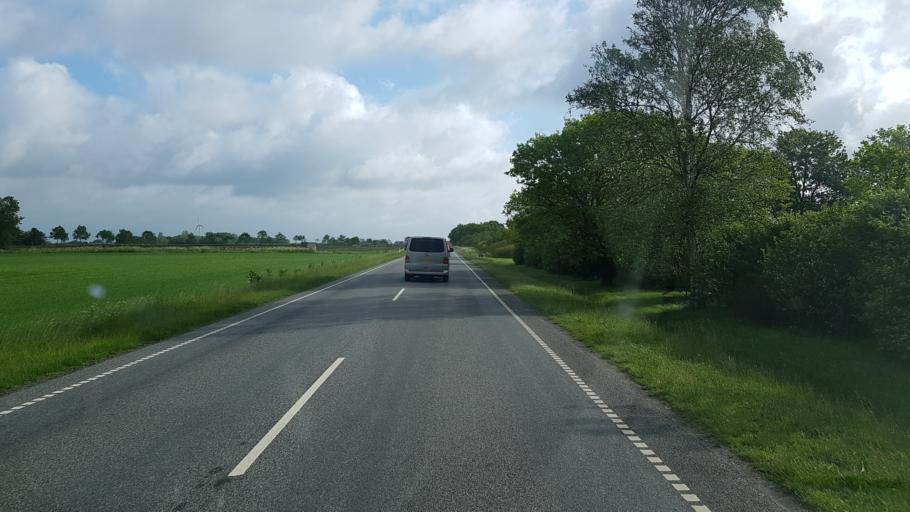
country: DK
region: South Denmark
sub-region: Vejen Kommune
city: Vejen
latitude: 55.4140
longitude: 9.1350
